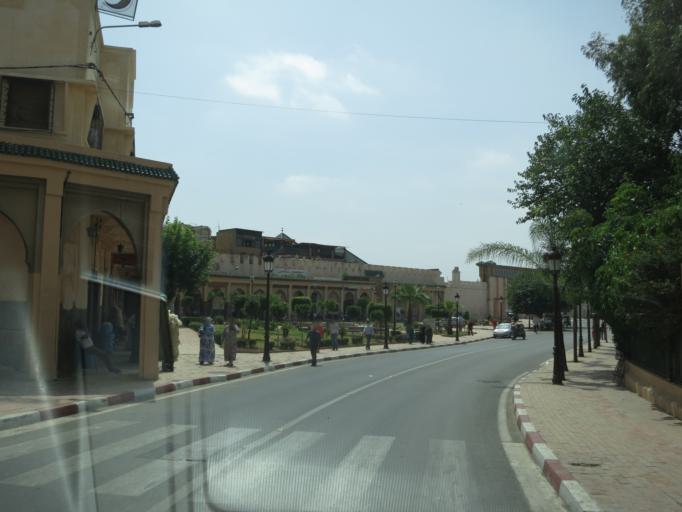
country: MA
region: Meknes-Tafilalet
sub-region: Meknes
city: Meknes
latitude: 33.8918
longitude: -5.5638
